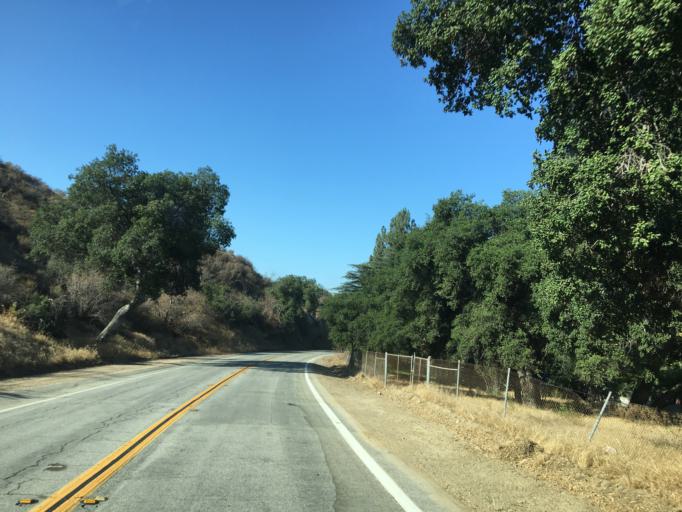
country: US
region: California
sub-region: Los Angeles County
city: San Fernando
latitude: 34.3029
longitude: -118.3959
